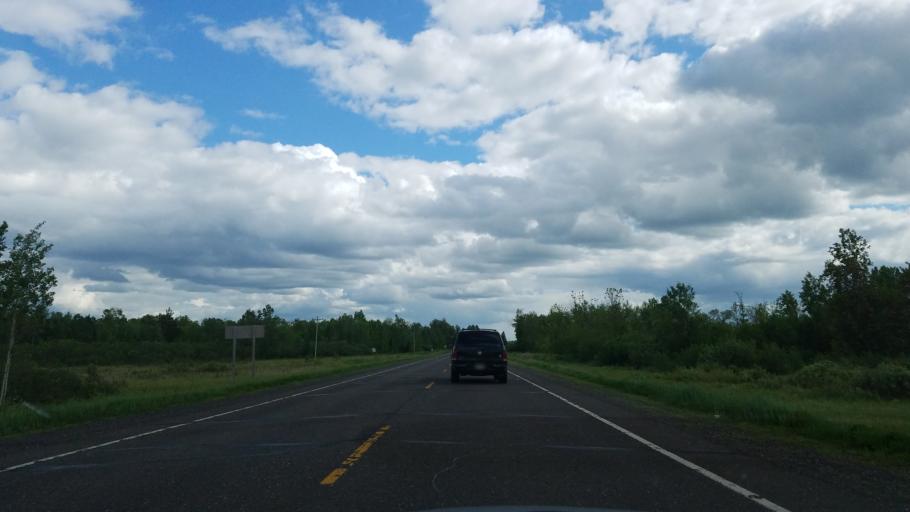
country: US
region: Wisconsin
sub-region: Burnett County
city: Siren
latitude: 46.1604
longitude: -92.2380
